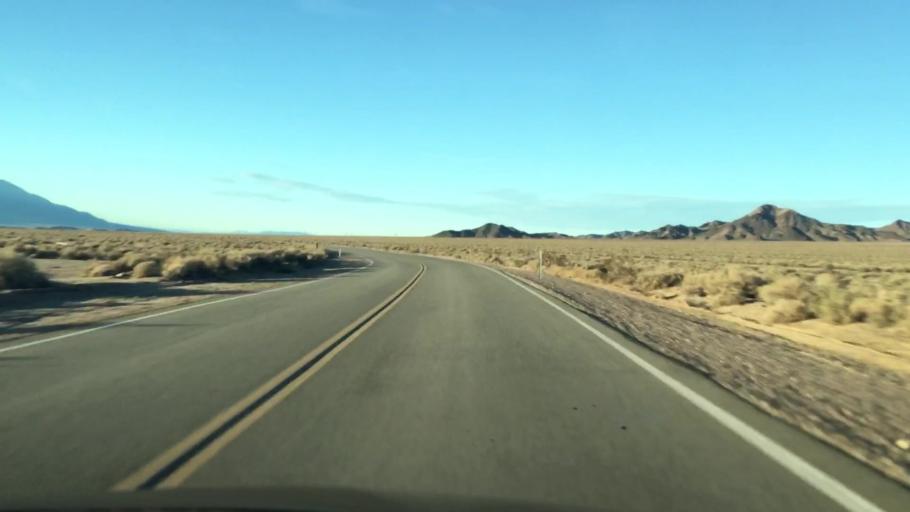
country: US
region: California
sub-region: San Bernardino County
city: Fort Irwin
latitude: 35.3439
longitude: -116.0837
